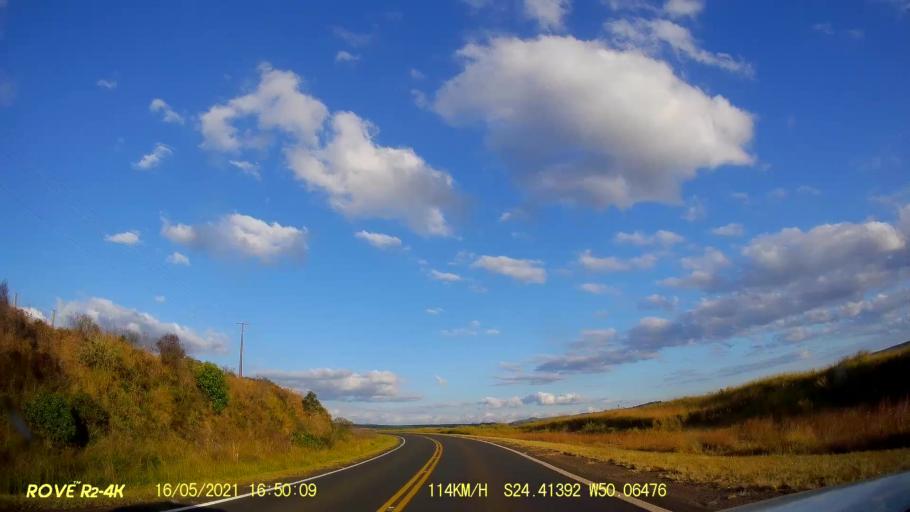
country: BR
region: Parana
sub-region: Pirai Do Sul
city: Pirai do Sul
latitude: -24.4140
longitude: -50.0648
